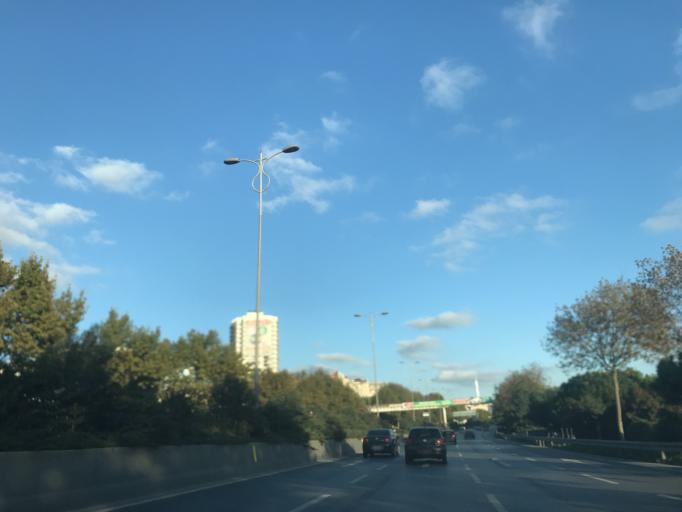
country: TR
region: Istanbul
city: Esenler
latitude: 41.0535
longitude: 28.8644
